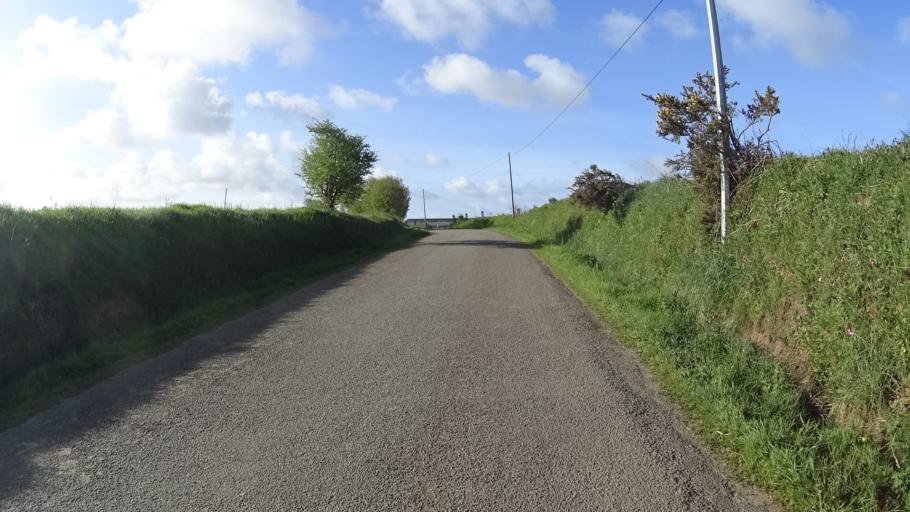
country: FR
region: Brittany
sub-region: Departement du Finistere
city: Ploumoguer
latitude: 48.4183
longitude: -4.6890
